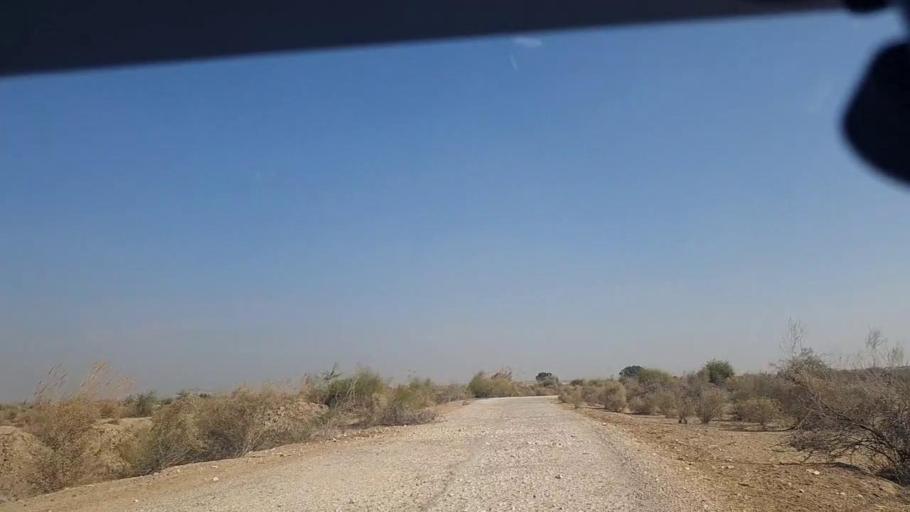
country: PK
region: Sindh
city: Khanpur
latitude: 27.5638
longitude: 69.3201
